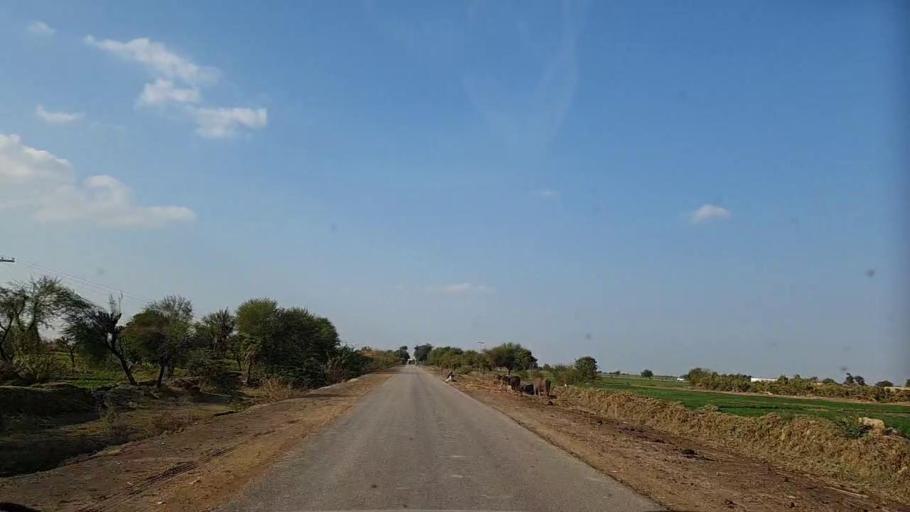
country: PK
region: Sindh
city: Tando Mittha Khan
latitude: 25.7298
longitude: 69.2128
